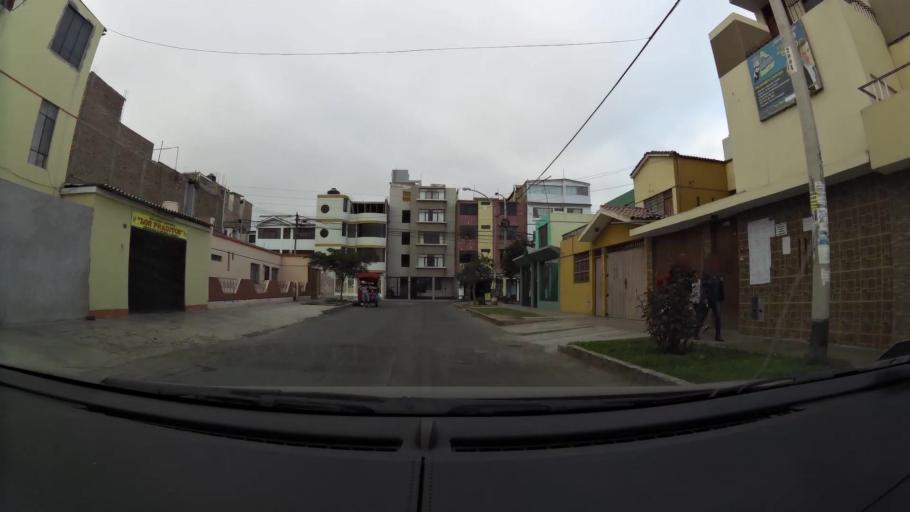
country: PE
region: La Libertad
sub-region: Provincia de Trujillo
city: Trujillo
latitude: -8.0974
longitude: -79.0263
